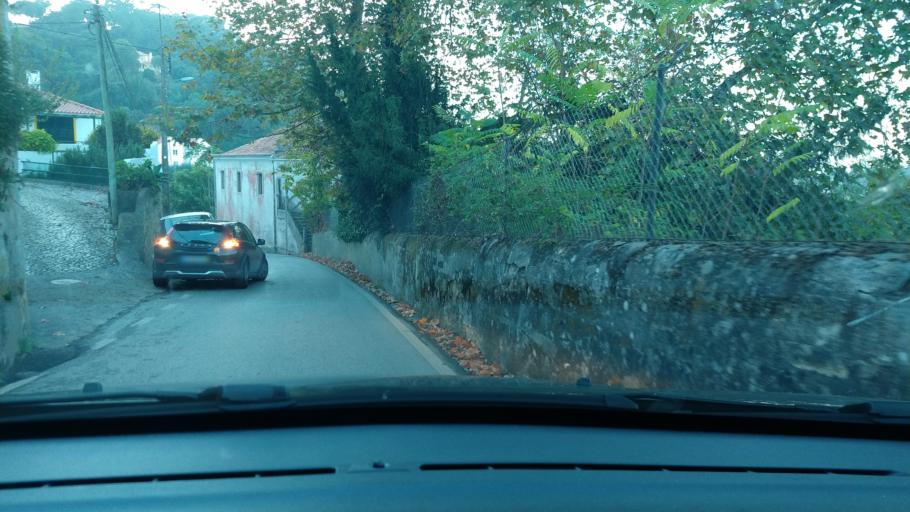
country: PT
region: Lisbon
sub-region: Sintra
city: Colares
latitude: 38.7951
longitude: -9.4342
